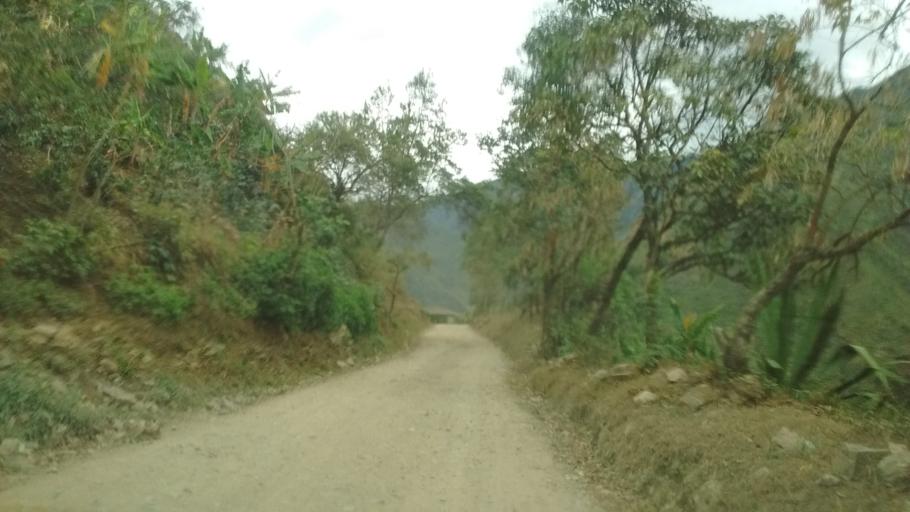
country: CO
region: Cauca
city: La Vega
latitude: 2.0459
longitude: -76.8019
